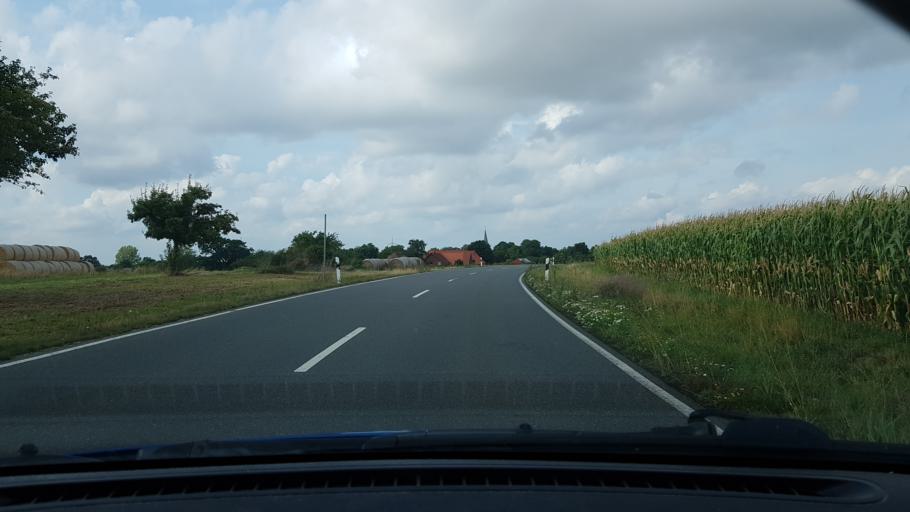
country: DE
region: Lower Saxony
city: Egestorf
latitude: 52.2955
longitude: 9.5054
